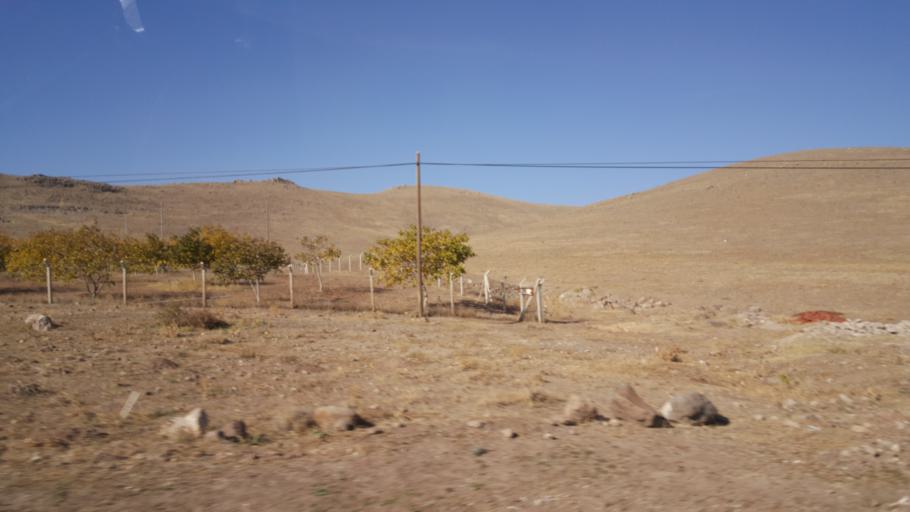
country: TR
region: Ankara
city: Altpinar
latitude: 39.1707
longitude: 32.6958
